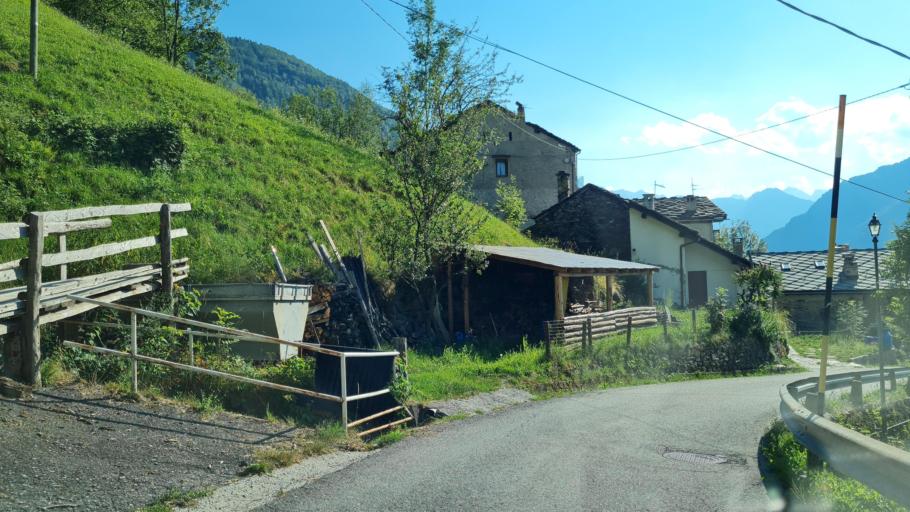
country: IT
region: Aosta Valley
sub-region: Valle d'Aosta
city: Lillianes
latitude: 45.6279
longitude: 7.8505
